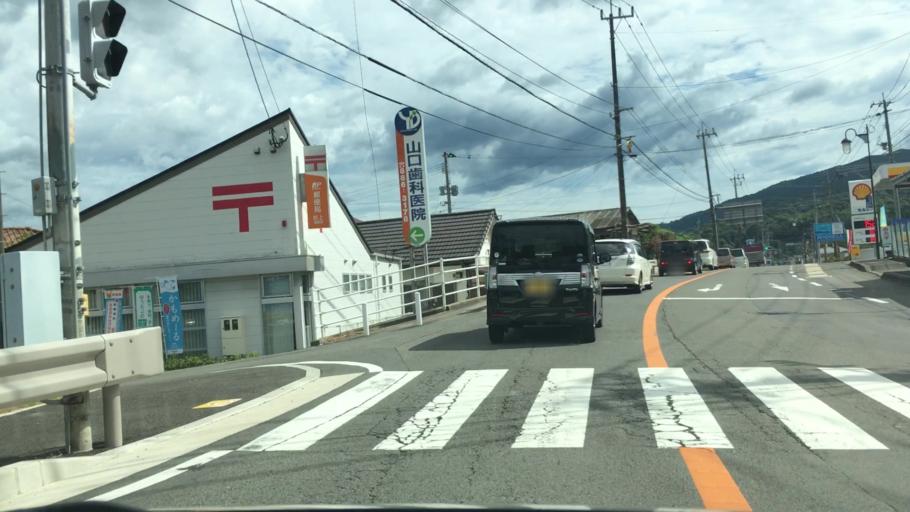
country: JP
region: Nagasaki
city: Togitsu
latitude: 32.9499
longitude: 129.7853
